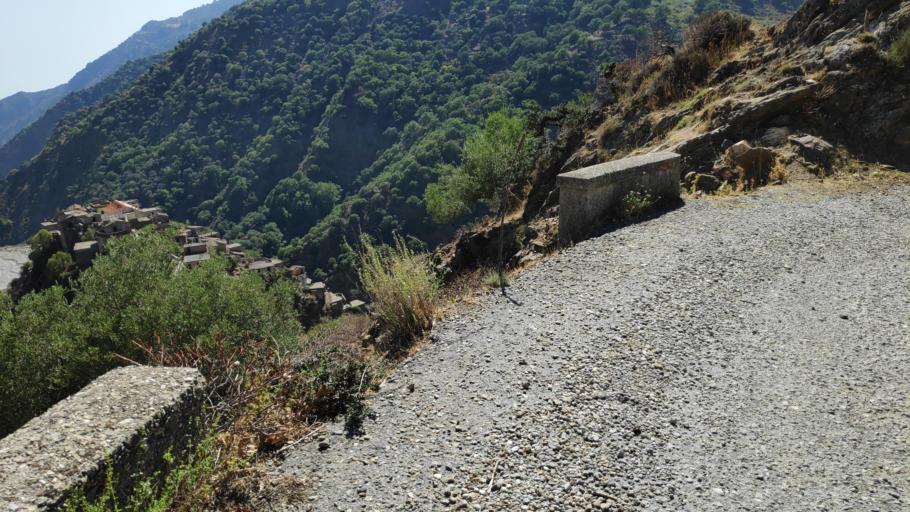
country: IT
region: Calabria
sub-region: Provincia di Reggio Calabria
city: Roccaforte del Greco
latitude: 38.0513
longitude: 15.9184
